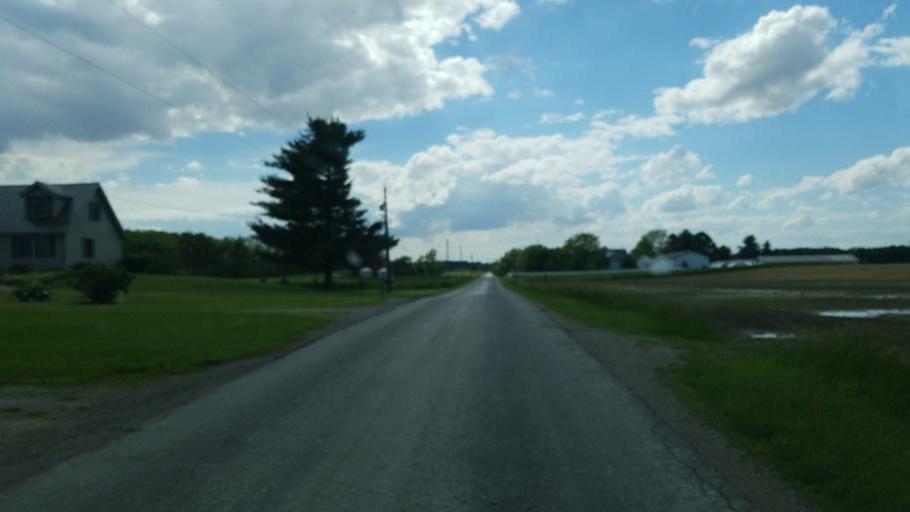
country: US
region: Ohio
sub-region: Huron County
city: Plymouth
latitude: 40.9698
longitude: -82.6327
